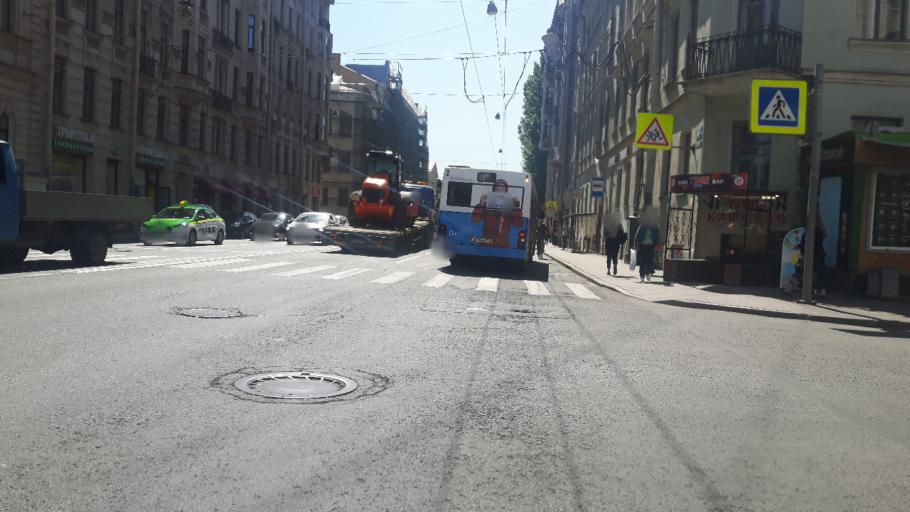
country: RU
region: St.-Petersburg
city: Admiralteisky
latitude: 59.9130
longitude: 30.2973
